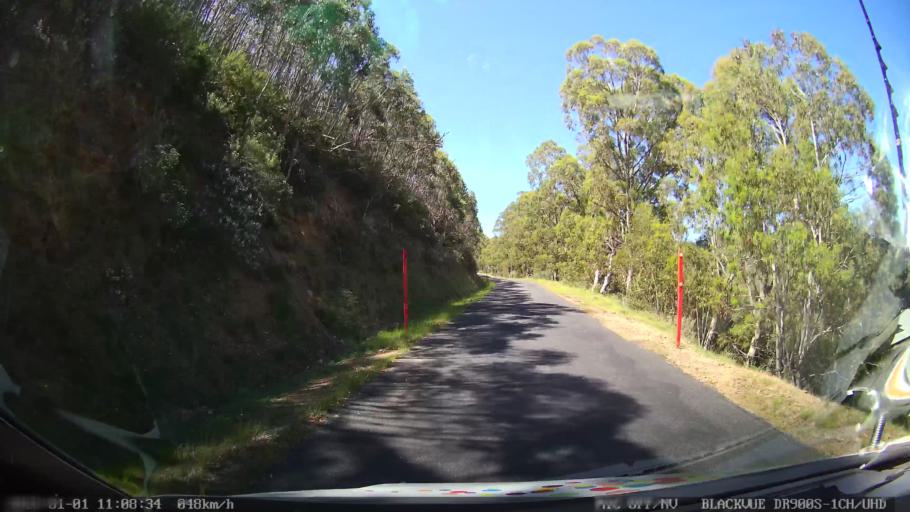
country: AU
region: New South Wales
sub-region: Snowy River
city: Jindabyne
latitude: -35.9605
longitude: 148.3946
